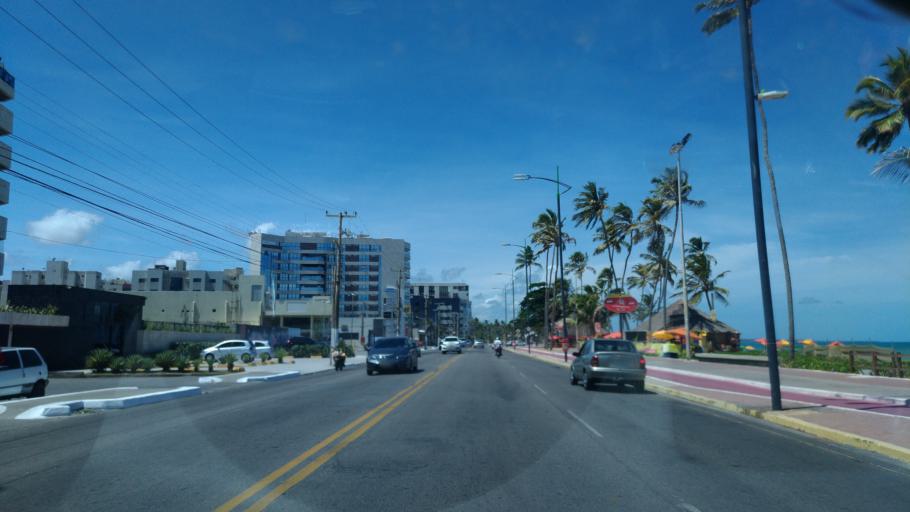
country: BR
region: Alagoas
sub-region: Maceio
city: Maceio
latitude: -9.6469
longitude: -35.7001
